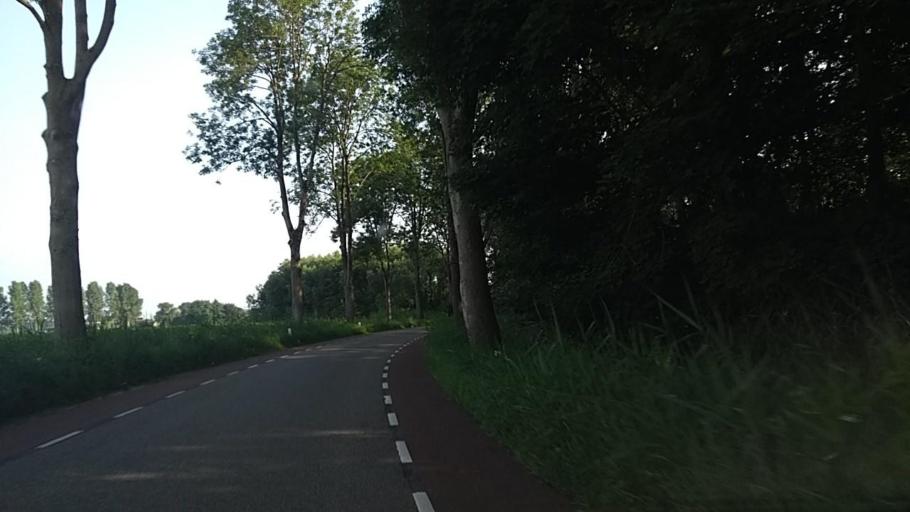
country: NL
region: Overijssel
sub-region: Gemeente Zwartewaterland
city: Hasselt
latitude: 52.5569
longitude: 6.1303
